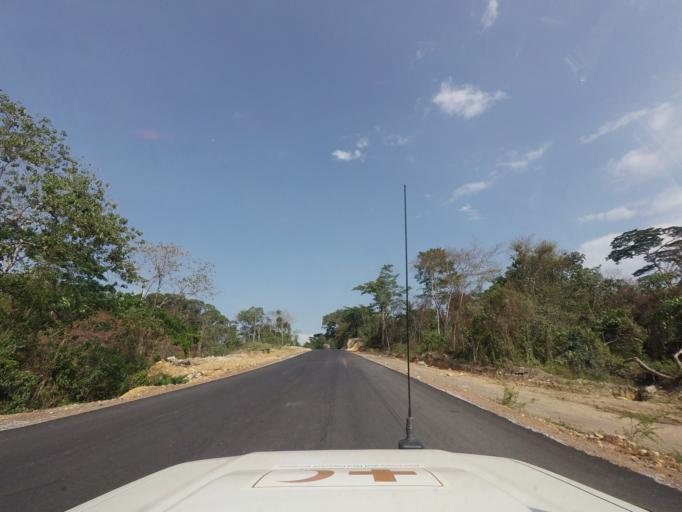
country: LR
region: Margibi
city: Kakata
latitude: 6.7785
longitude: -9.9775
